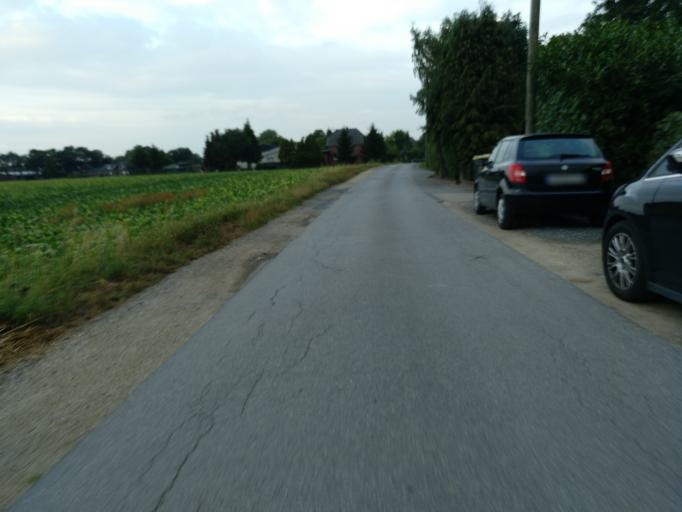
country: DE
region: North Rhine-Westphalia
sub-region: Regierungsbezirk Dusseldorf
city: Krefeld
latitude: 51.4089
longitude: 6.5566
